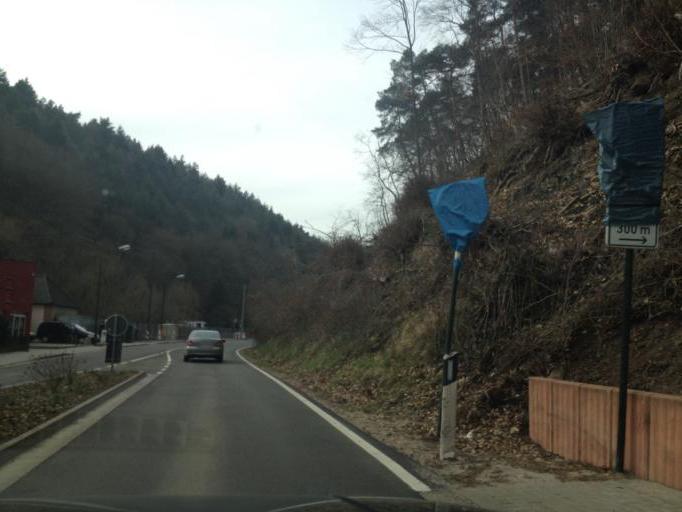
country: DE
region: Rheinland-Pfalz
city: Bad Duerkheim
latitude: 49.4636
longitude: 8.1221
